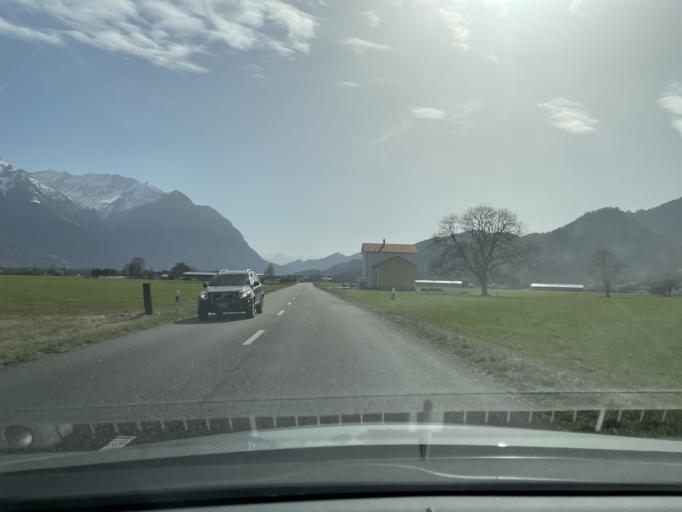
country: CH
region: Saint Gallen
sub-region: Wahlkreis Werdenberg
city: Sevelen
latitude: 47.1386
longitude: 9.4849
